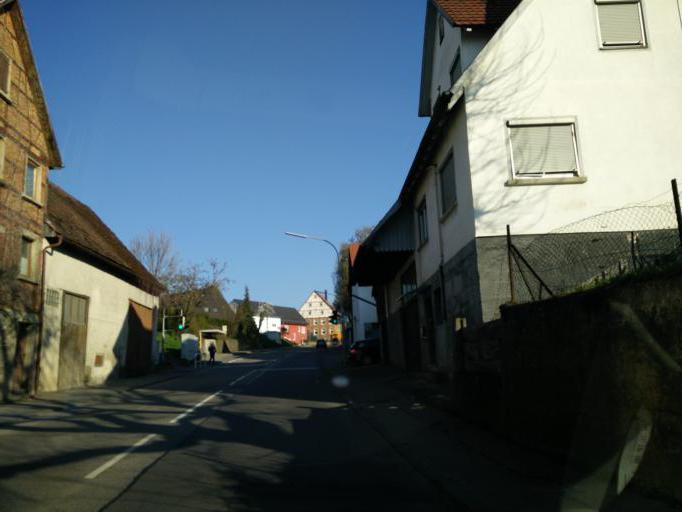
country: DE
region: Baden-Wuerttemberg
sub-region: Regierungsbezirk Stuttgart
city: Deckenpfronn
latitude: 48.6245
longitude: 8.8344
